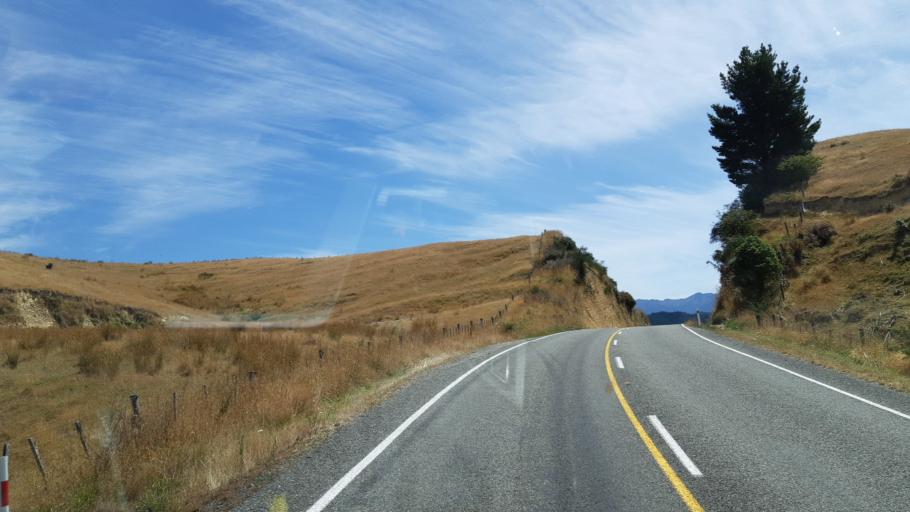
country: NZ
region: Tasman
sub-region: Tasman District
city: Wakefield
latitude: -41.3432
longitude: 172.8167
